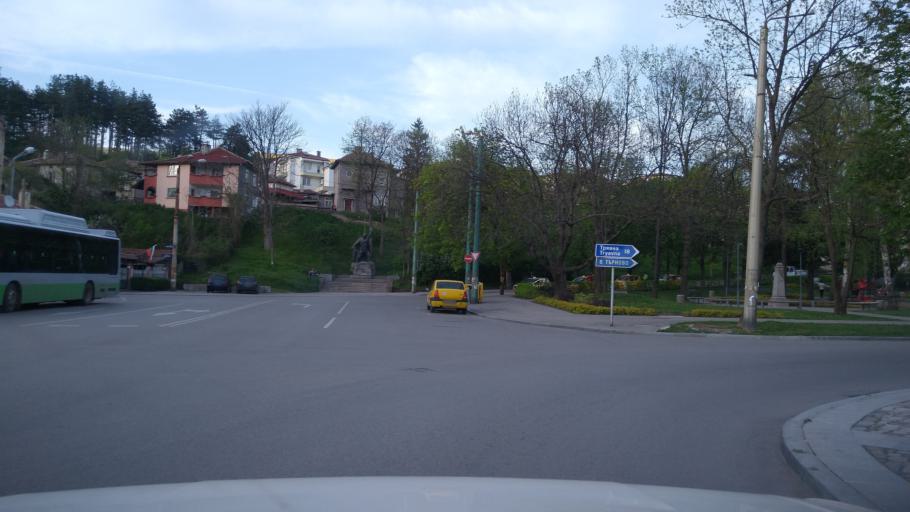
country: BG
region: Gabrovo
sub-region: Obshtina Gabrovo
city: Gabrovo
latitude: 42.8615
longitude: 25.3226
